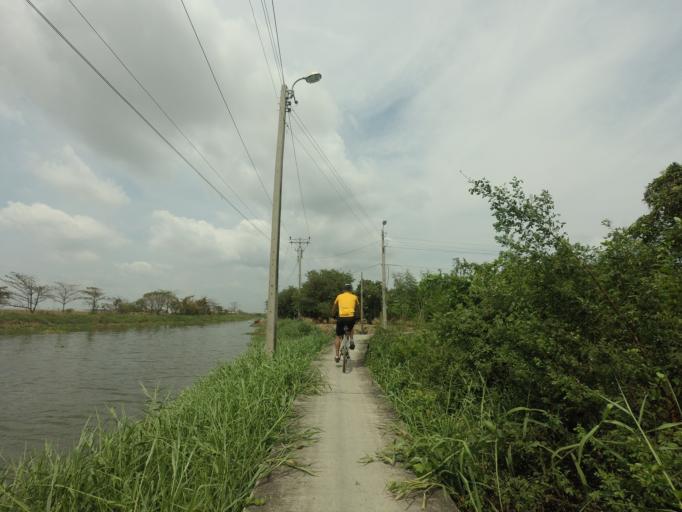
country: TH
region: Bangkok
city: Lat Krabang
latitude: 13.6674
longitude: 100.7627
